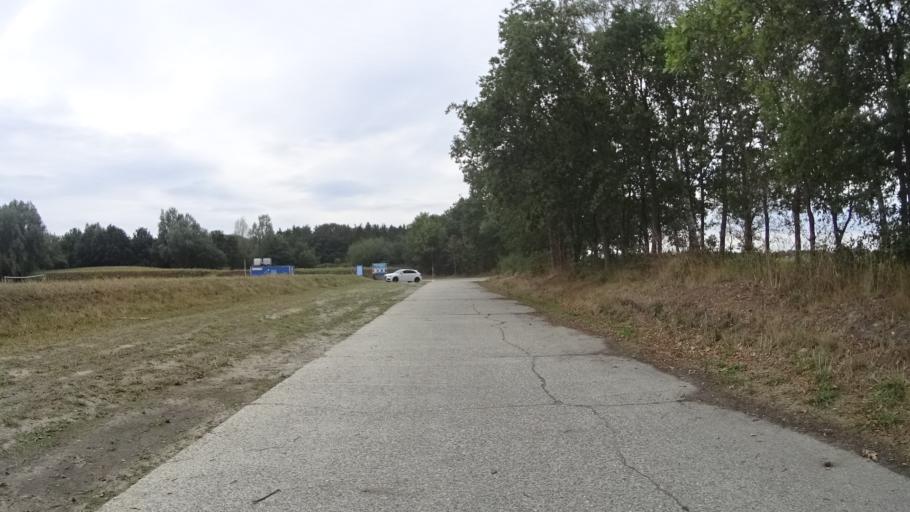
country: NL
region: Groningen
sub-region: Gemeente Slochteren
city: Slochteren
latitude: 53.1810
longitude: 6.8508
